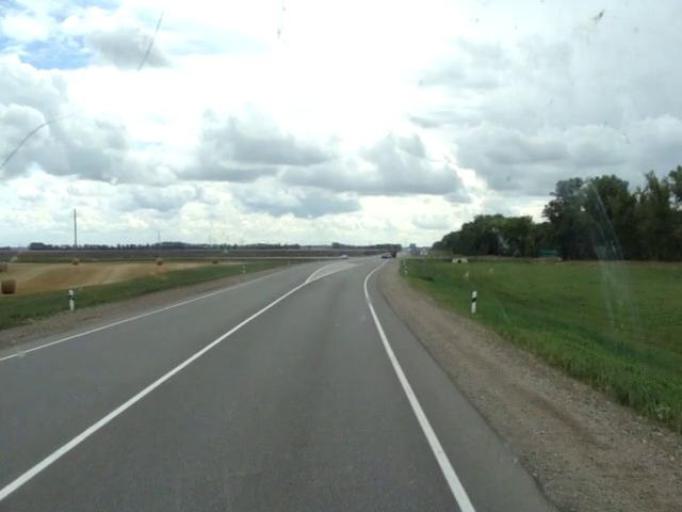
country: RU
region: Altai Krai
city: Shubenka
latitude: 52.6779
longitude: 85.0501
